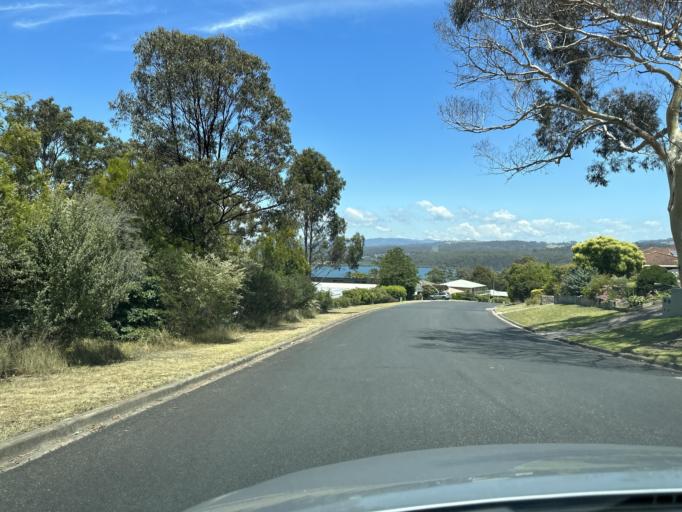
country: AU
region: New South Wales
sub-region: Bega Valley
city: Merimbula
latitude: -36.8915
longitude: 149.8959
